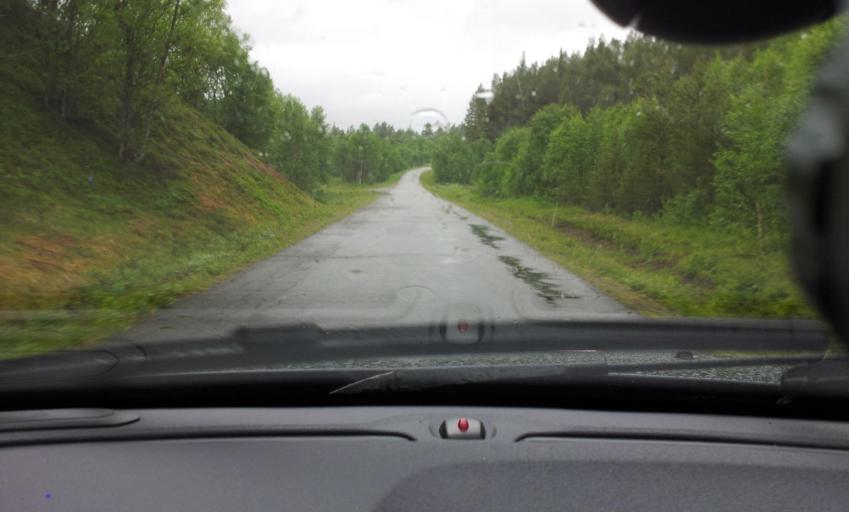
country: SE
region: Jaemtland
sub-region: Are Kommun
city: Are
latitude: 63.1510
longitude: 12.9257
